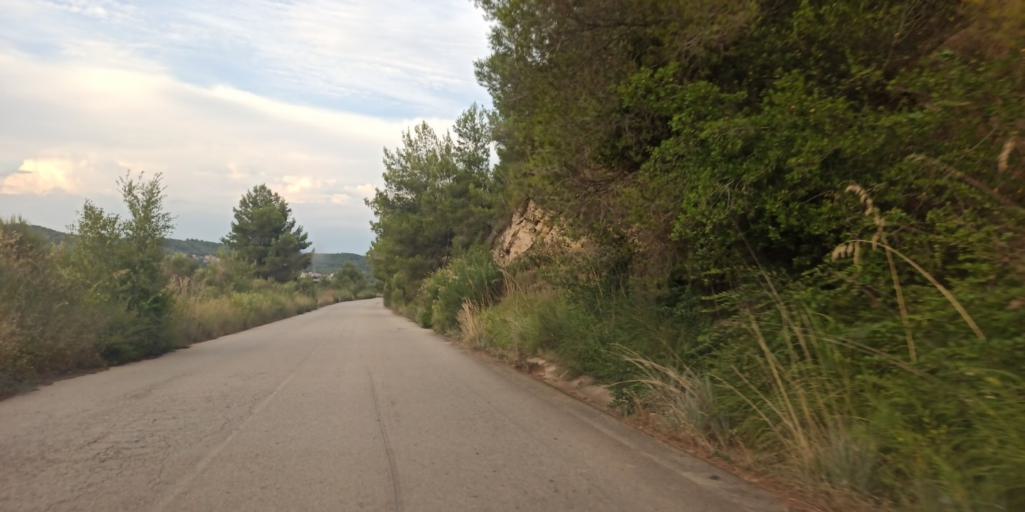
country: ES
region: Catalonia
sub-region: Provincia de Barcelona
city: Castelldefels
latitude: 41.2931
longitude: 1.9635
